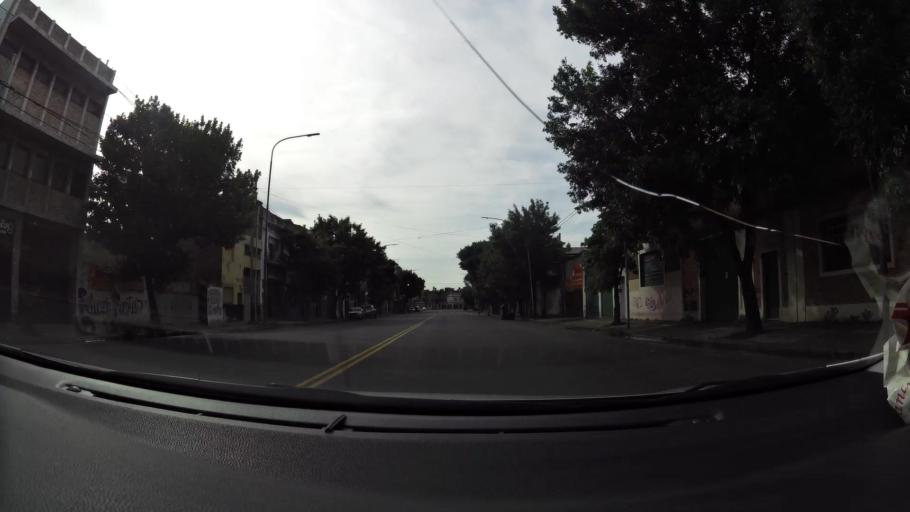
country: AR
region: Buenos Aires F.D.
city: Villa Lugano
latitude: -34.6465
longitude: -58.4304
